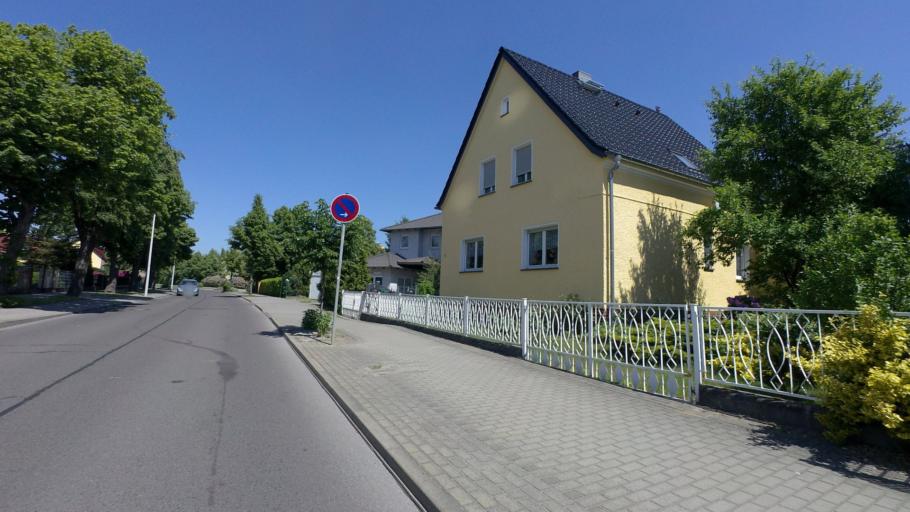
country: DE
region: Brandenburg
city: Cottbus
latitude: 51.7826
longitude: 14.3376
